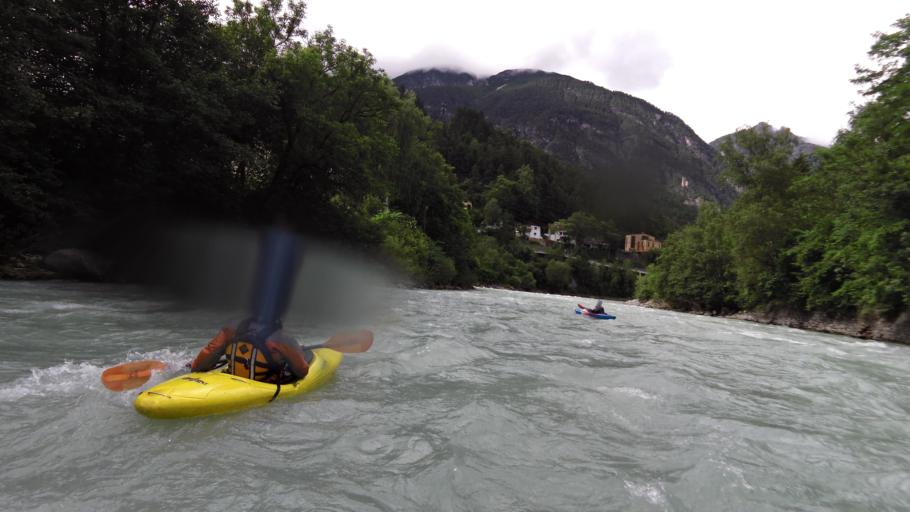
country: AT
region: Tyrol
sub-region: Politischer Bezirk Landeck
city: Landeck
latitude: 47.1427
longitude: 10.5651
